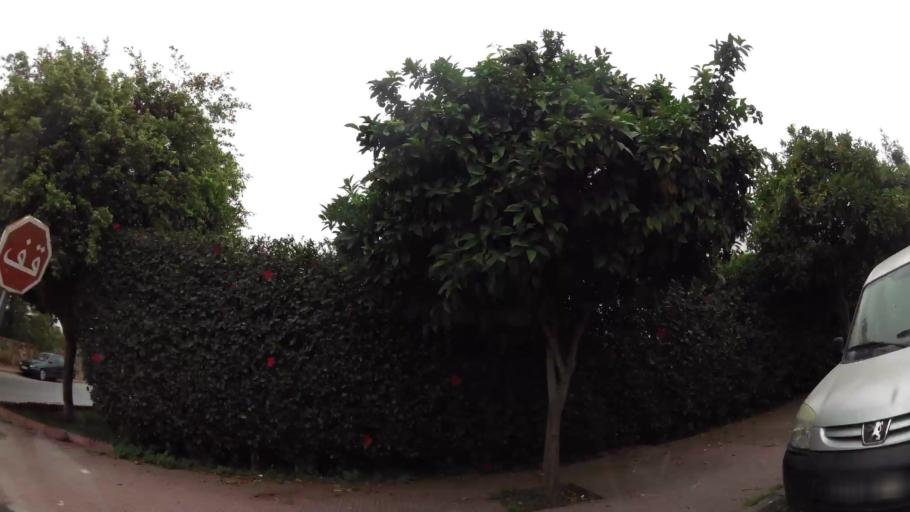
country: MA
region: Rabat-Sale-Zemmour-Zaer
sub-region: Rabat
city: Rabat
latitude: 33.9708
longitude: -6.8228
